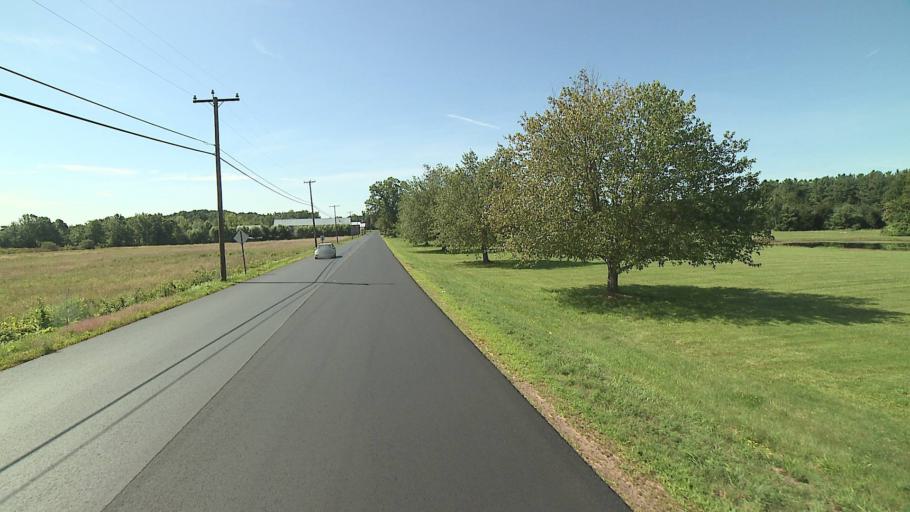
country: US
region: Connecticut
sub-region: Hartford County
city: Suffield Depot
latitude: 41.9832
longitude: -72.7059
